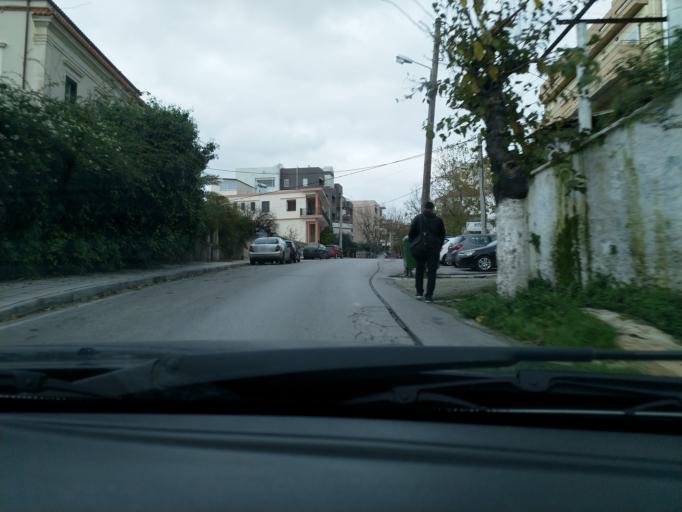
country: GR
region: Crete
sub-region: Nomos Chanias
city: Chania
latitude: 35.5103
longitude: 24.0338
